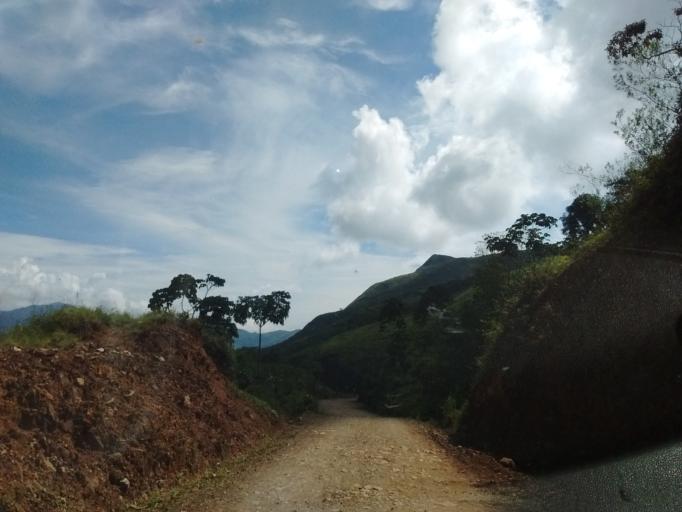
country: CO
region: Cauca
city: Morales
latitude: 2.6883
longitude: -76.7477
